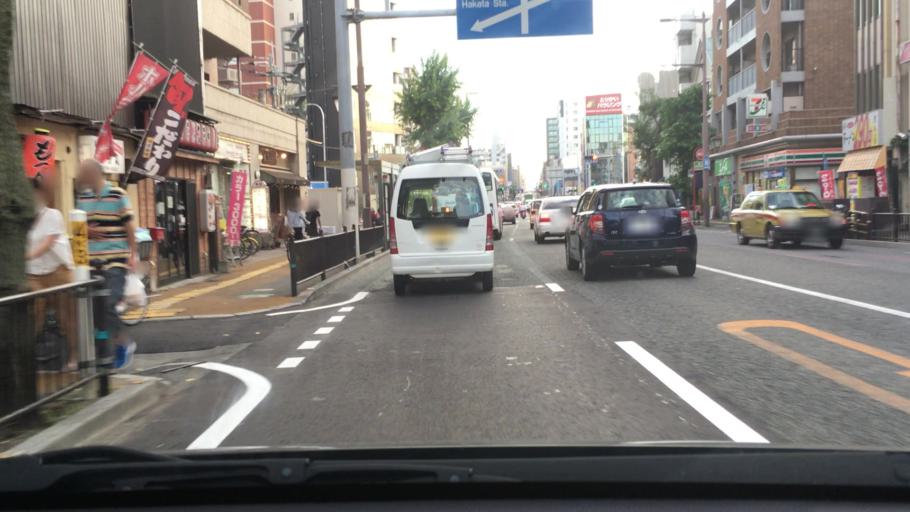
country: JP
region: Fukuoka
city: Fukuoka-shi
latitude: 33.5789
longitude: 130.3798
